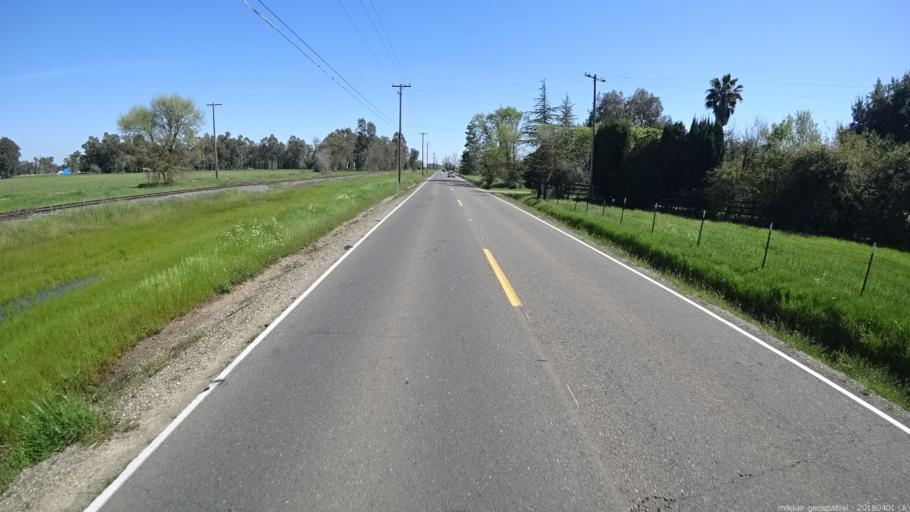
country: US
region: California
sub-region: Sacramento County
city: Wilton
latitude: 38.4047
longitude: -121.2621
